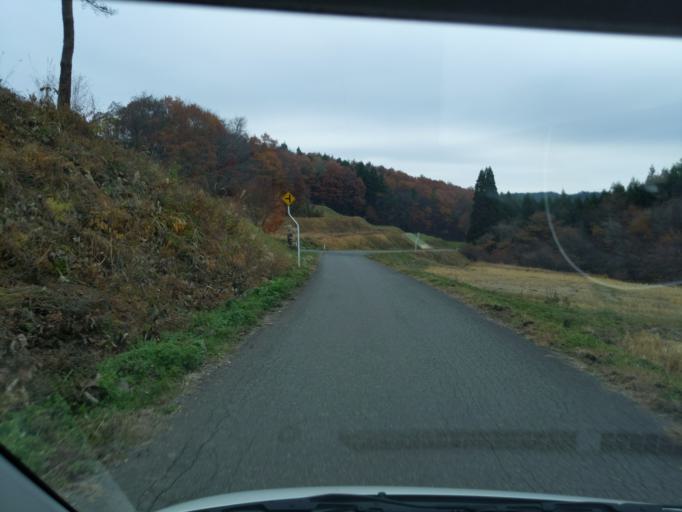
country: JP
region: Iwate
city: Ichinoseki
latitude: 39.0022
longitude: 141.0275
